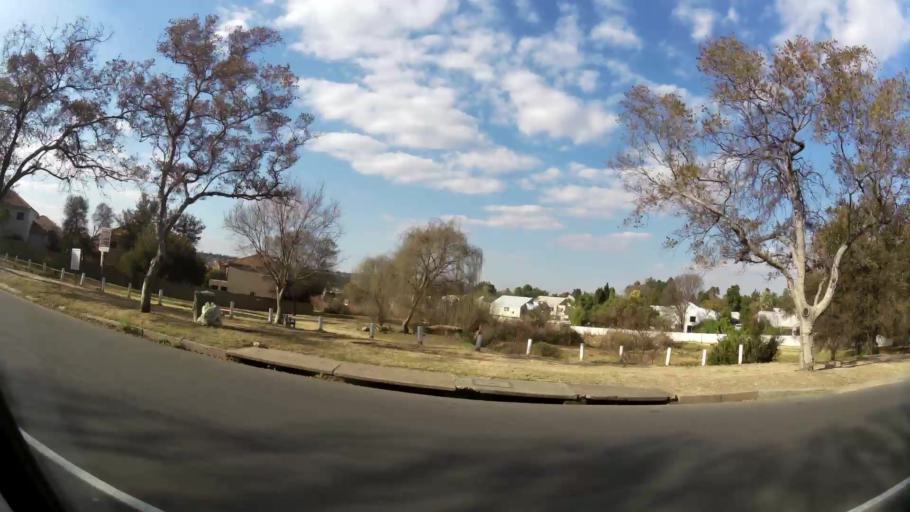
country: ZA
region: Gauteng
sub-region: City of Johannesburg Metropolitan Municipality
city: Diepsloot
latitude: -26.0125
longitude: 28.0308
